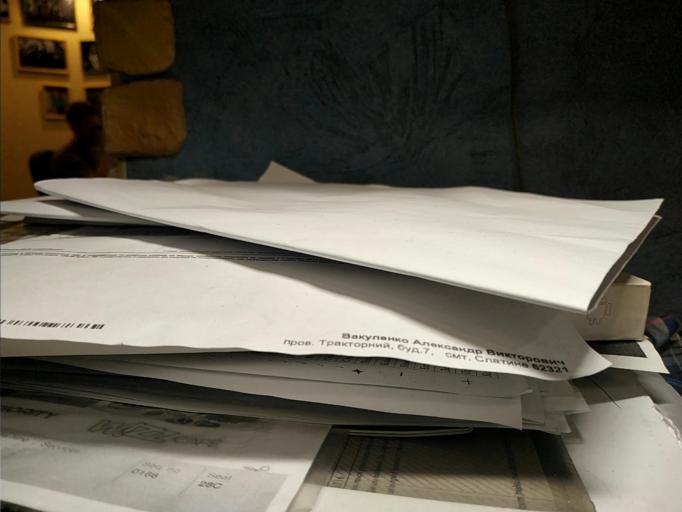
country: RU
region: Tverskaya
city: Zubtsov
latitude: 56.1113
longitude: 34.6245
